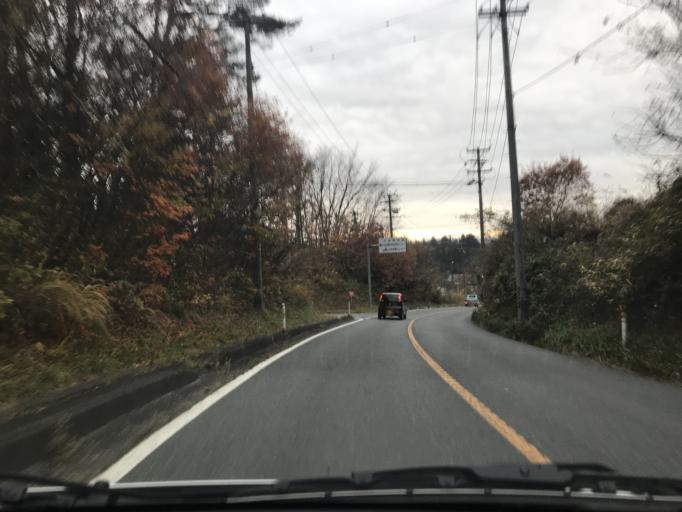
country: JP
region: Iwate
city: Ichinoseki
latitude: 39.0105
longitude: 141.3277
